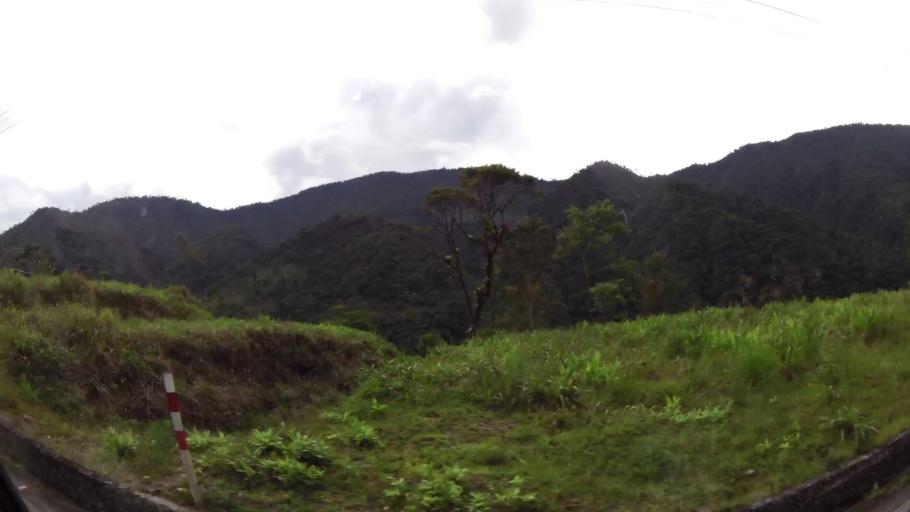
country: EC
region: Pastaza
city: Puyo
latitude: -1.4387
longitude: -78.1788
